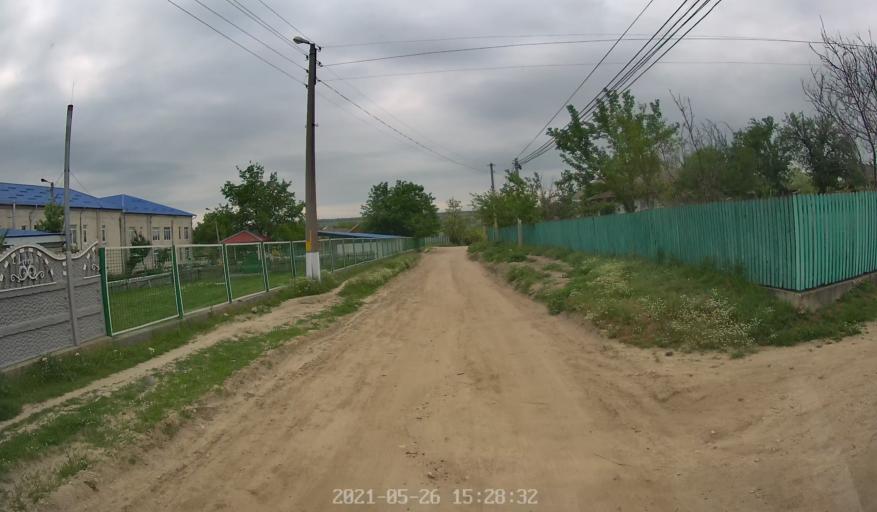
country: MD
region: Hincesti
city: Dancu
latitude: 46.6672
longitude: 28.3229
